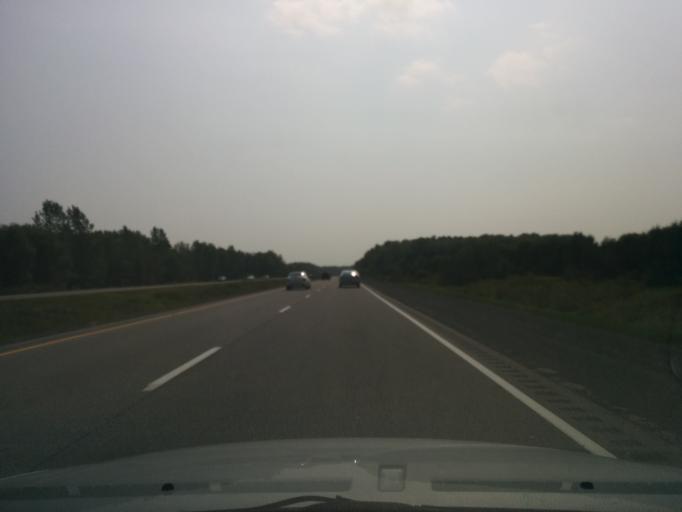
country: CA
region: Ontario
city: Bells Corners
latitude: 45.1717
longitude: -75.6996
